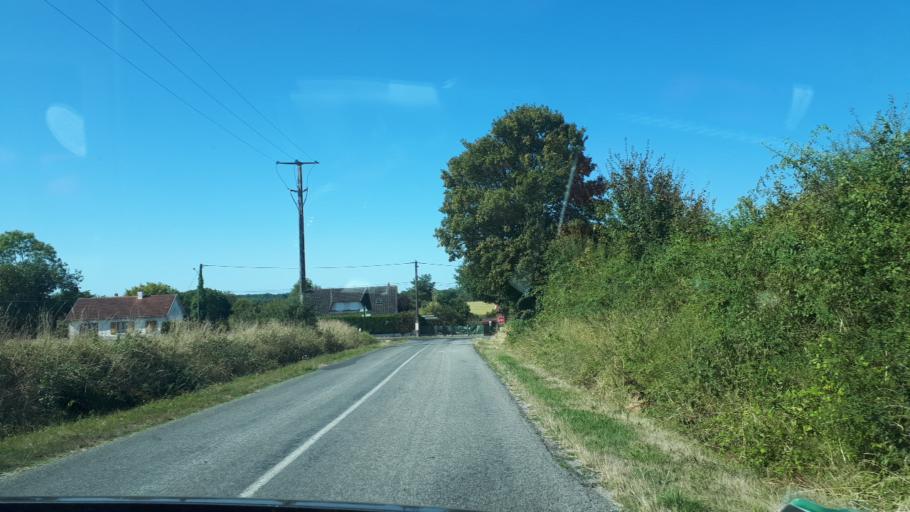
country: FR
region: Centre
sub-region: Departement du Loiret
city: Autry-le-Chatel
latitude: 47.5927
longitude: 2.6090
